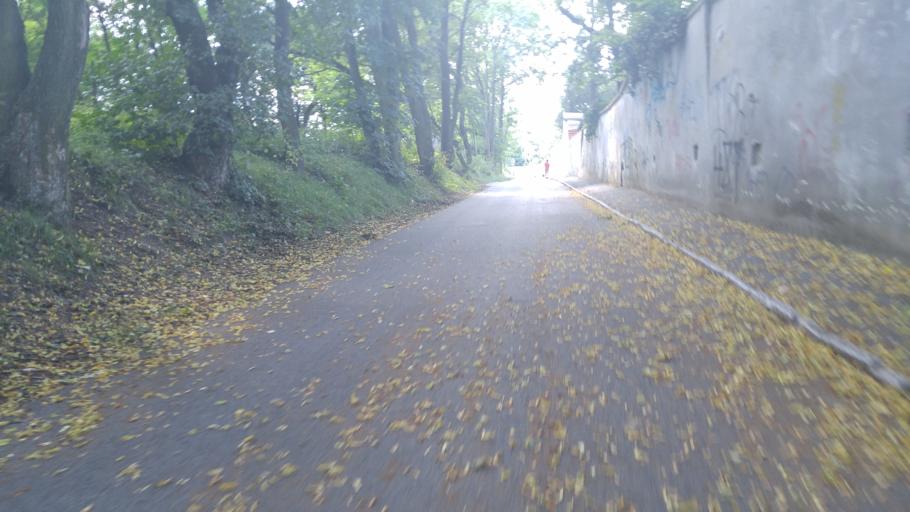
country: CZ
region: Central Bohemia
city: Horomerice
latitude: 50.0850
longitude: 14.3535
